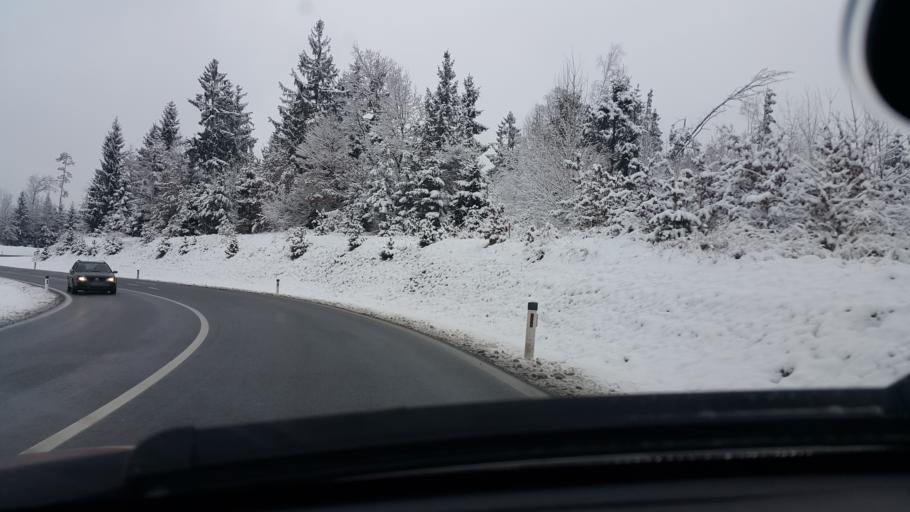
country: AT
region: Styria
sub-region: Politischer Bezirk Voitsberg
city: Mooskirchen
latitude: 47.0037
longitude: 15.2689
